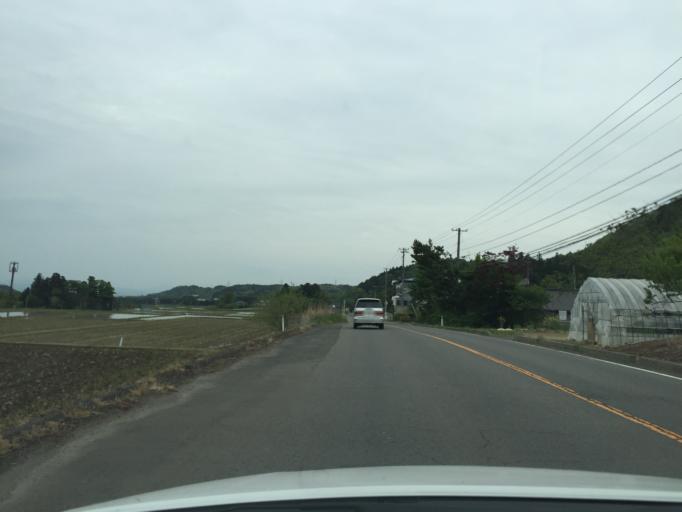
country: JP
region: Fukushima
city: Motomiya
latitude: 37.5038
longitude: 140.2757
